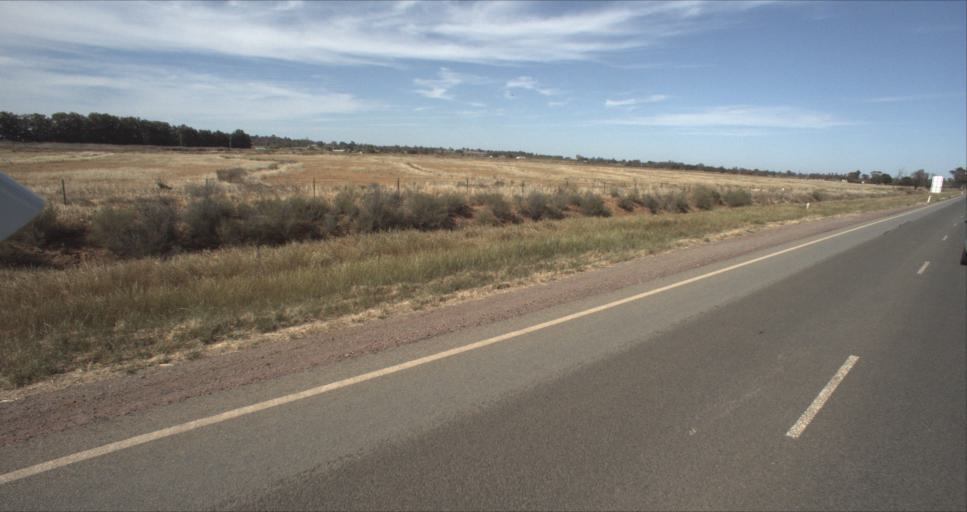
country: AU
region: New South Wales
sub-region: Leeton
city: Leeton
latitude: -34.5569
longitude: 146.4482
